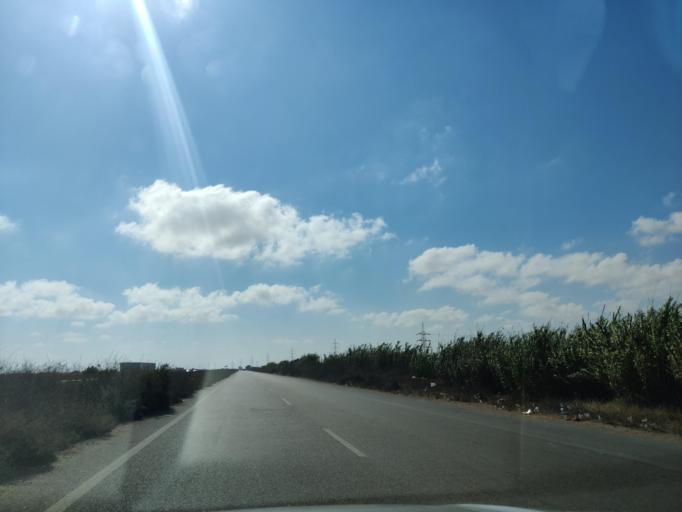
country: EG
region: Muhafazat Matruh
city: Al `Alamayn
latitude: 31.0569
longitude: 28.2504
